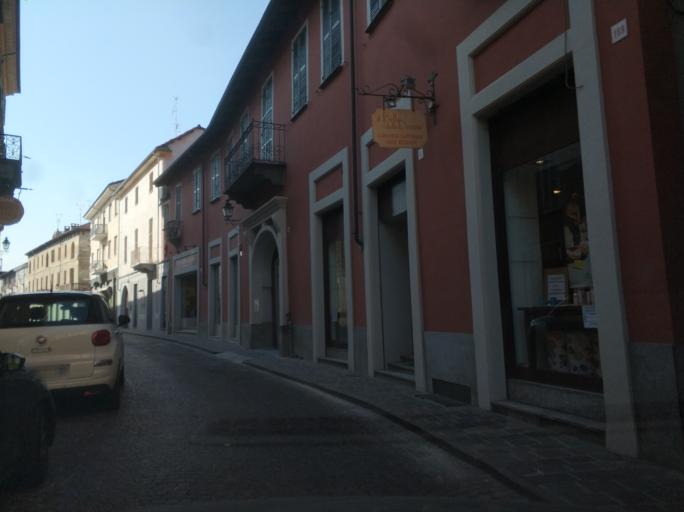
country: IT
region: Piedmont
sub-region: Provincia di Cuneo
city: Bra
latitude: 44.6978
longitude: 7.8529
